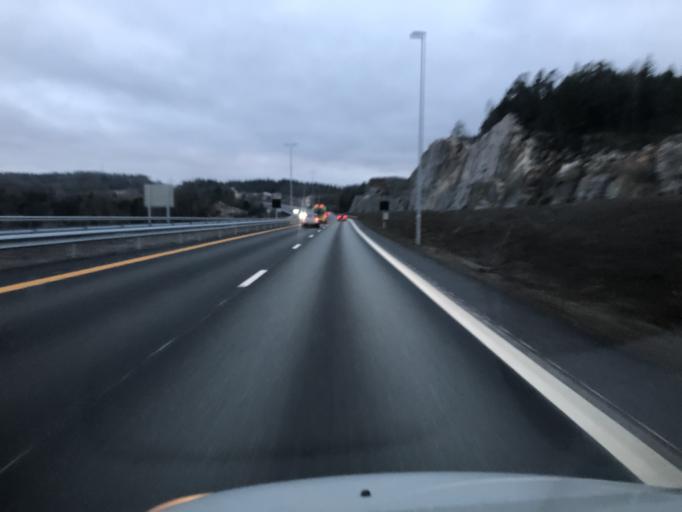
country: NO
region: Aust-Agder
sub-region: Arendal
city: Arendal
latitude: 58.5170
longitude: 8.8326
